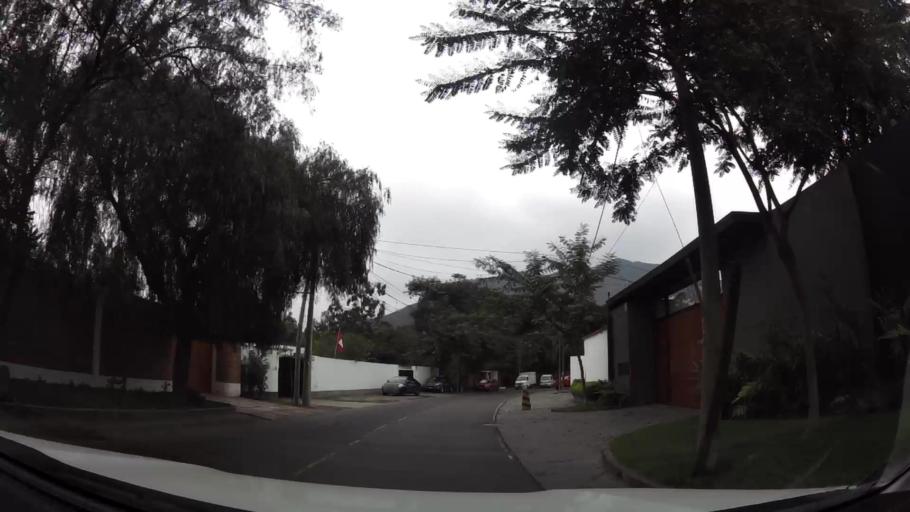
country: PE
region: Lima
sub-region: Lima
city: La Molina
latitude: -12.0792
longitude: -76.9143
